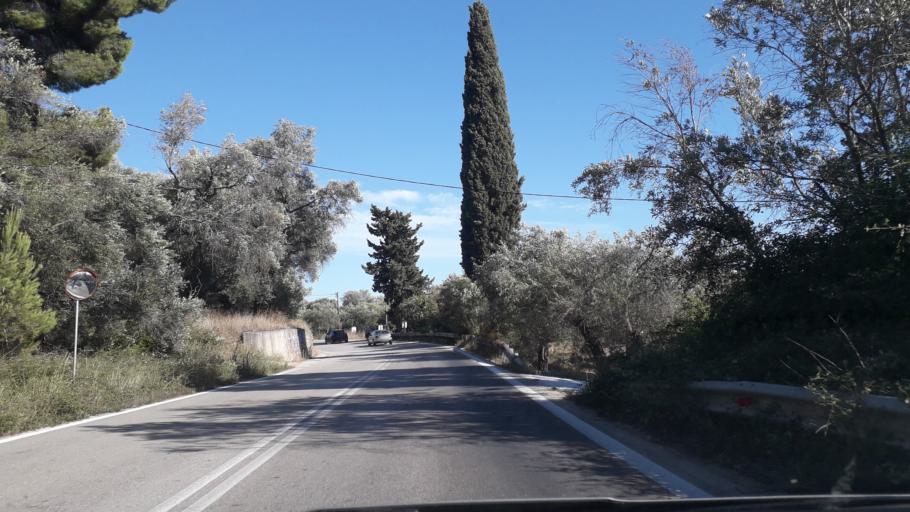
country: GR
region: Ionian Islands
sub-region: Nomos Kerkyras
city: Agios Matthaios
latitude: 39.4485
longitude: 19.9301
